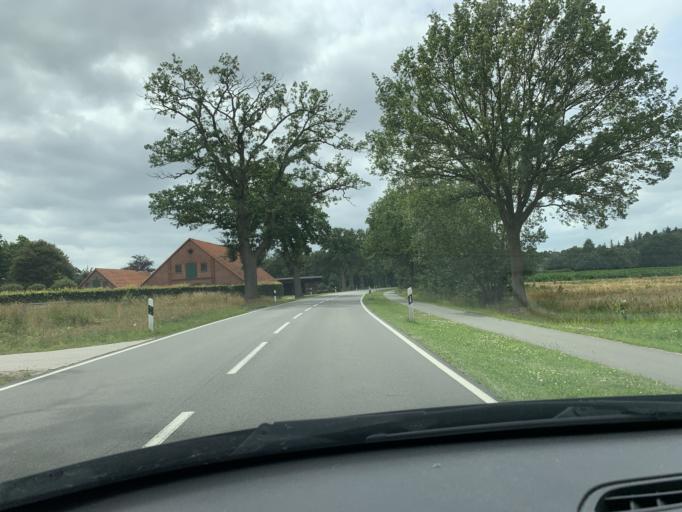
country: DE
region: Lower Saxony
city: Westerstede
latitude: 53.2723
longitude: 7.9503
